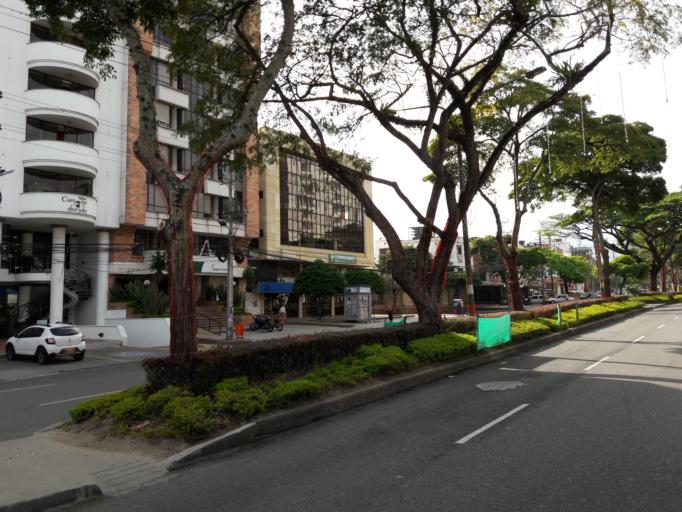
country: CO
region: Tolima
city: Ibague
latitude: 4.4375
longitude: -75.2157
